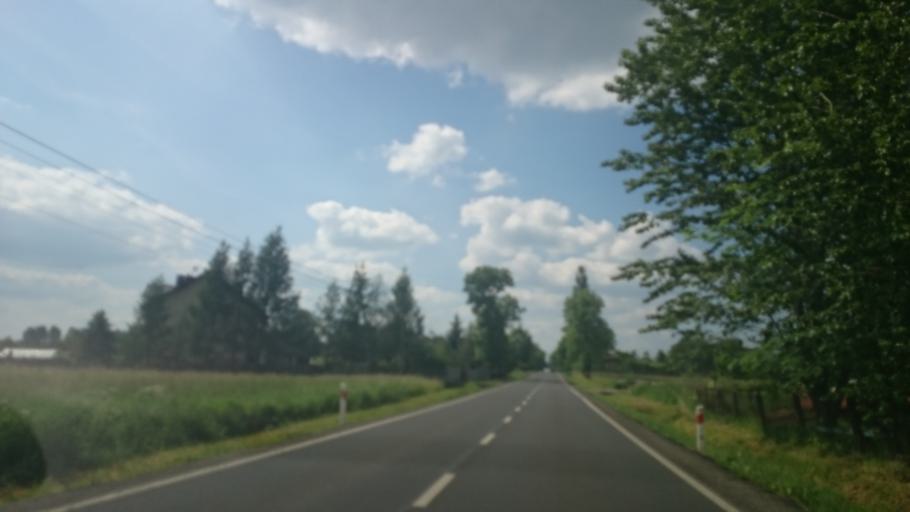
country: PL
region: Silesian Voivodeship
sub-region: Powiat myszkowski
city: Zarki
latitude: 50.6039
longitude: 19.4153
